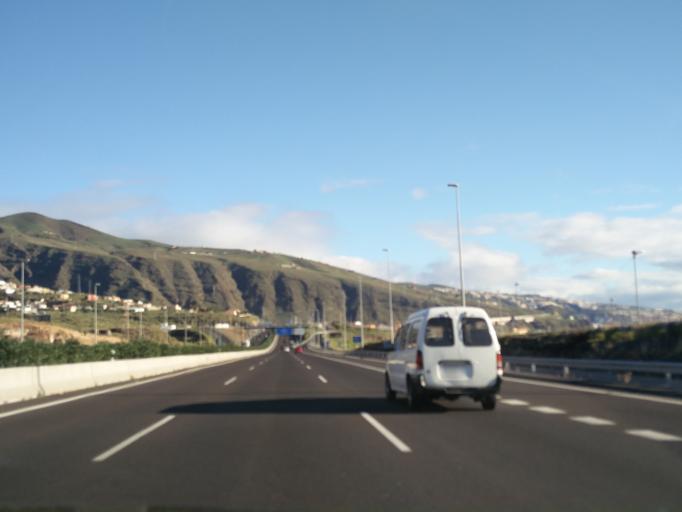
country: ES
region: Canary Islands
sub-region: Provincia de Santa Cruz de Tenerife
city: Candelaria
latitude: 28.3656
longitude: -16.3695
